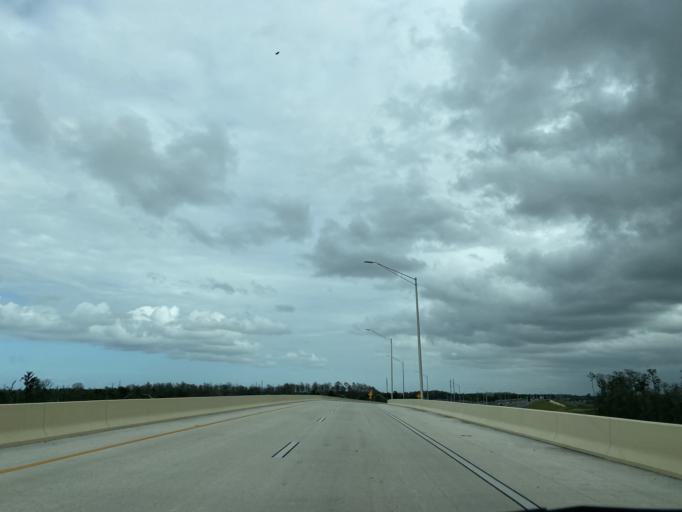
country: US
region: Florida
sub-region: Orange County
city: Wedgefield
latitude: 28.4506
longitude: -81.1689
